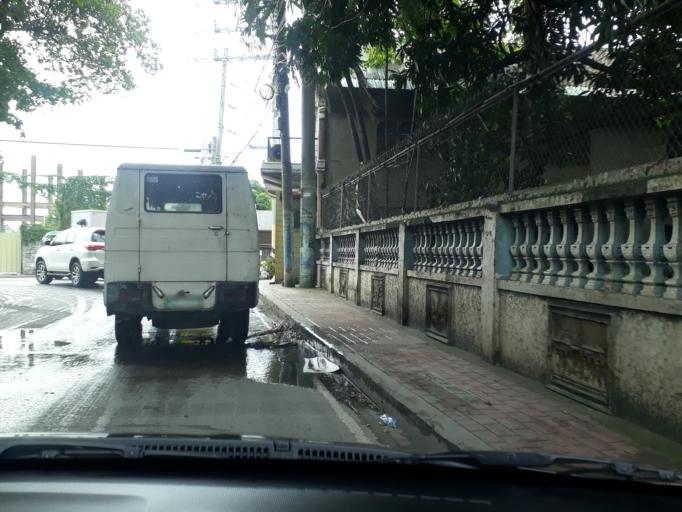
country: PH
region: Calabarzon
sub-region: Province of Rizal
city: Valenzuela
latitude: 14.7169
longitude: 120.9783
